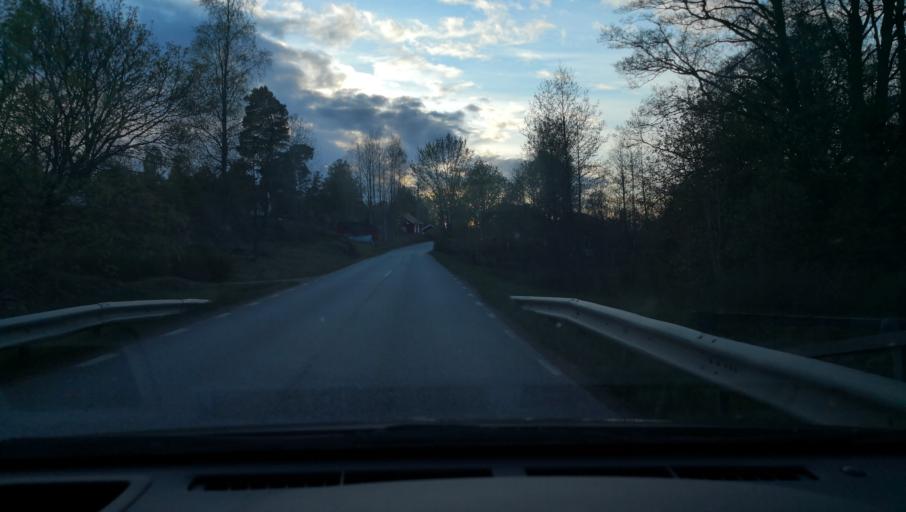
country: SE
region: OErebro
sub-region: Askersunds Kommun
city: Asbro
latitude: 58.9254
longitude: 15.0377
